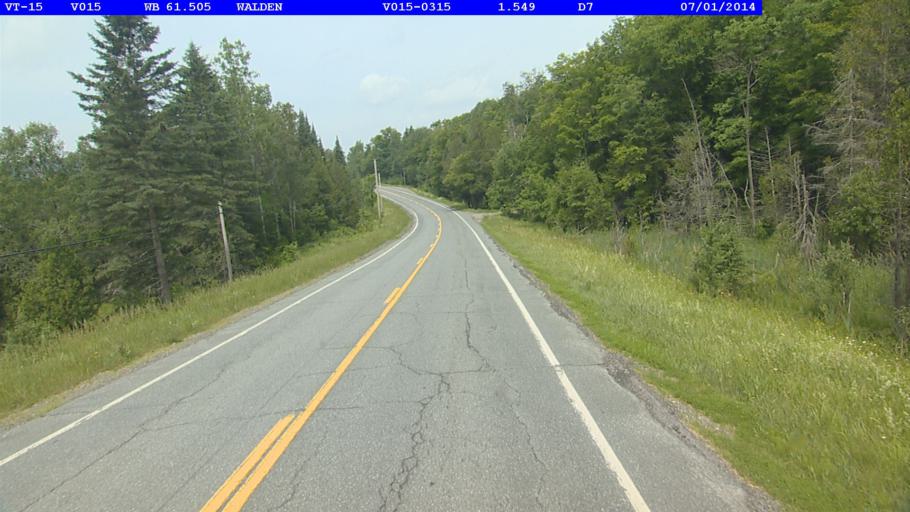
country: US
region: Vermont
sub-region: Caledonia County
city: Hardwick
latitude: 44.4718
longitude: -72.2817
